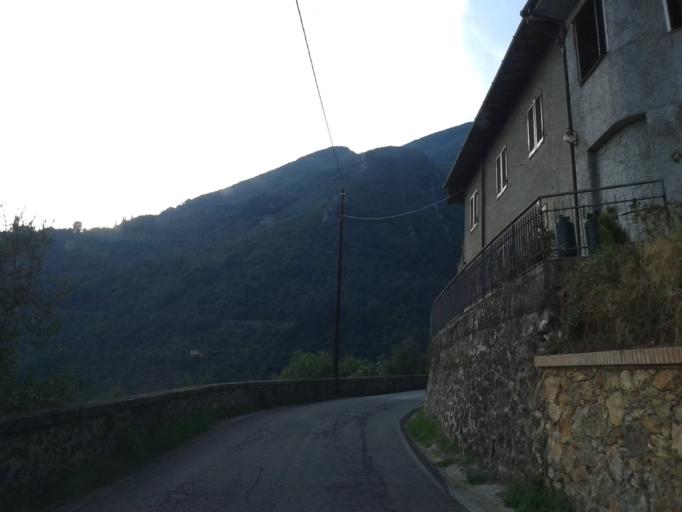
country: IT
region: Tuscany
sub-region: Provincia di Lucca
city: Pontestazzemese
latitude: 43.9538
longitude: 10.3104
